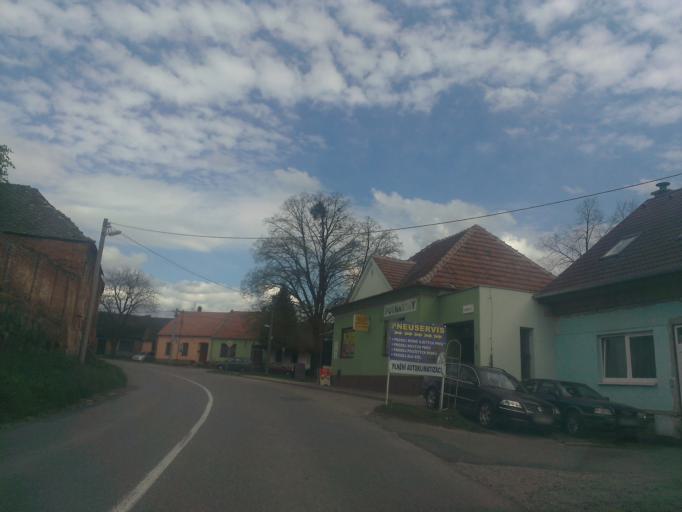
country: CZ
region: South Moravian
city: Dolni Kounice
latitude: 49.1049
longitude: 16.4670
